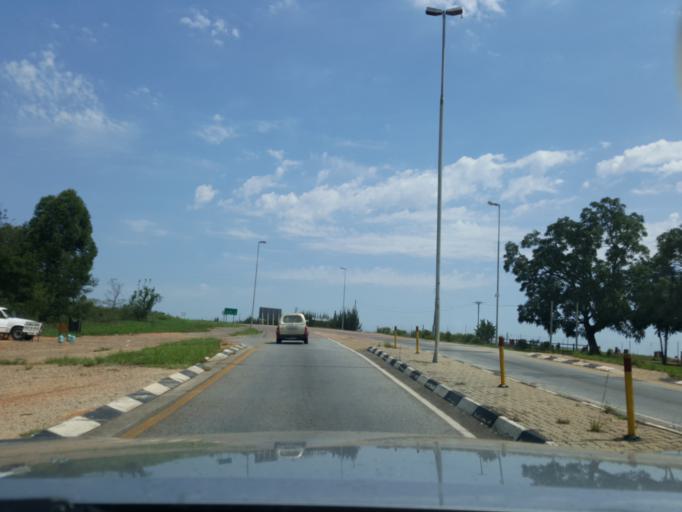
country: ZA
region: Mpumalanga
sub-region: Ehlanzeni District
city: White River
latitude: -25.3056
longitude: 31.0304
